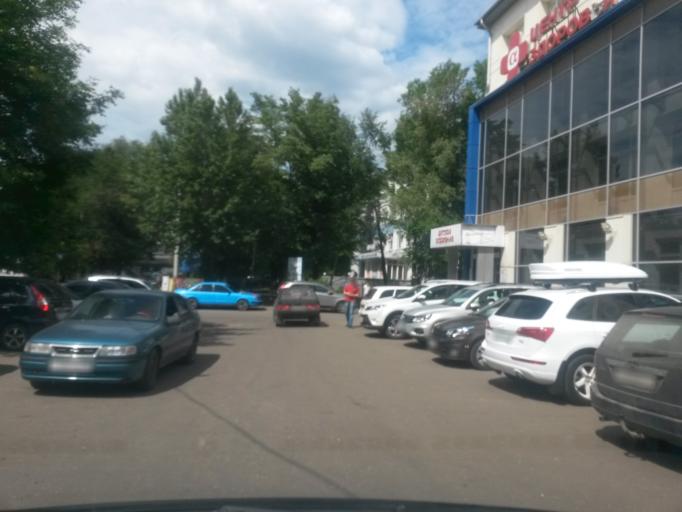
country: RU
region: Jaroslavl
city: Yaroslavl
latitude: 57.6423
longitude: 39.8753
